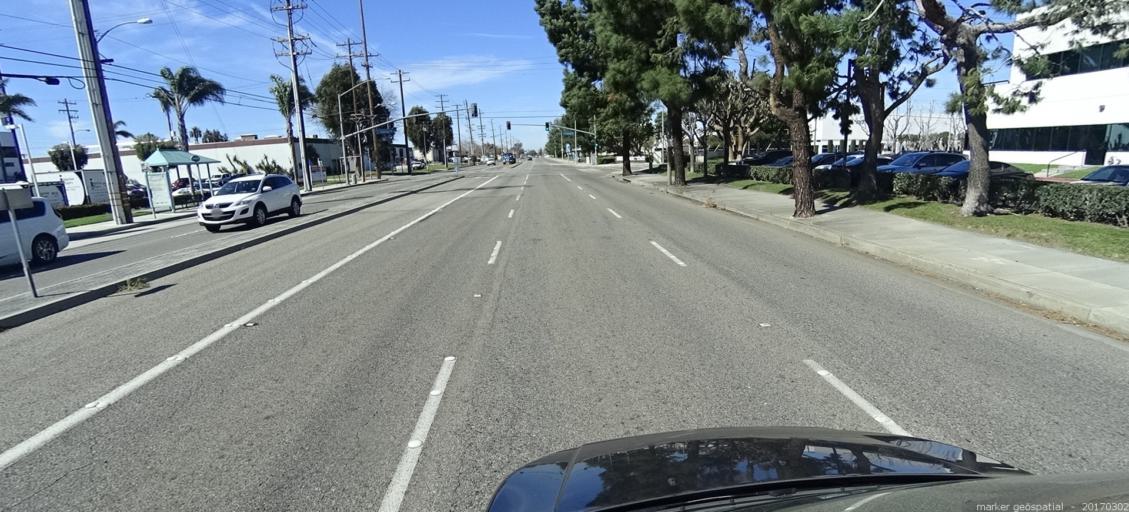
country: US
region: California
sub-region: Orange County
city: Yorba Linda
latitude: 33.8596
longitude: -117.8058
